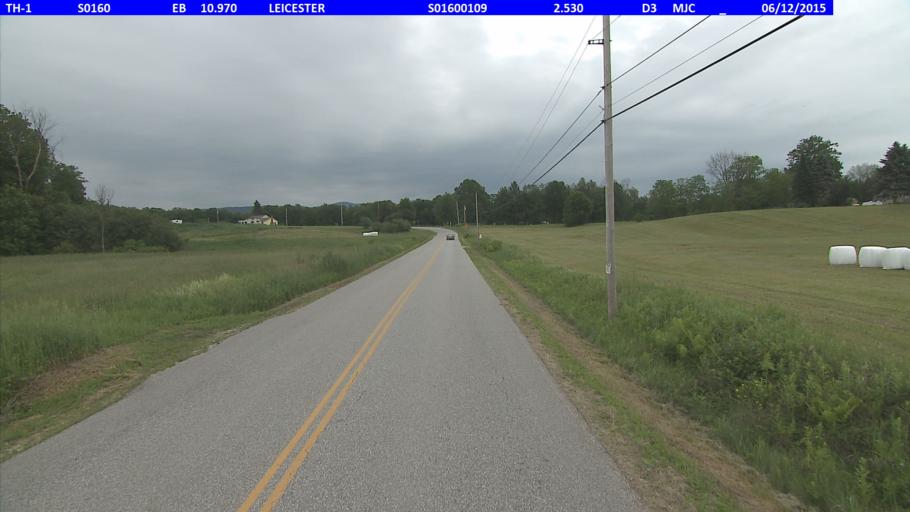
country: US
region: Vermont
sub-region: Rutland County
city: Brandon
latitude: 43.8615
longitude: -73.1171
